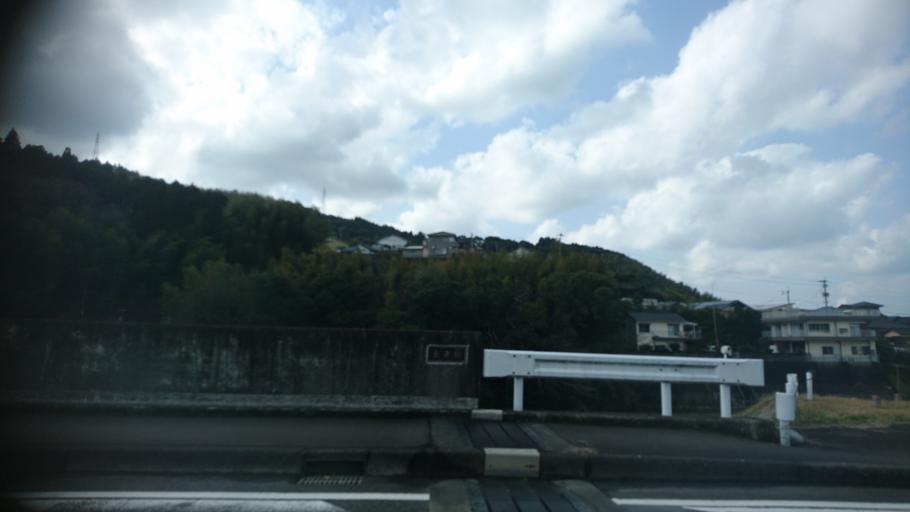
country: JP
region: Kagoshima
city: Satsumasendai
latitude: 31.8092
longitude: 130.3076
